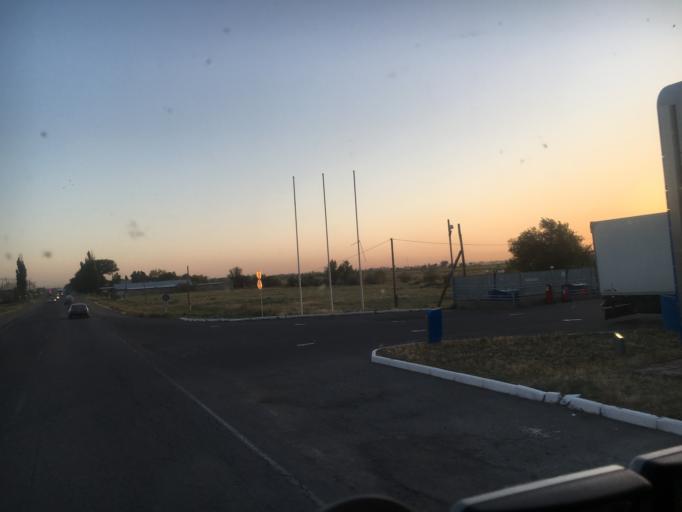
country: KZ
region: Zhambyl
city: Sarykemer
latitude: 42.9287
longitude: 71.4911
